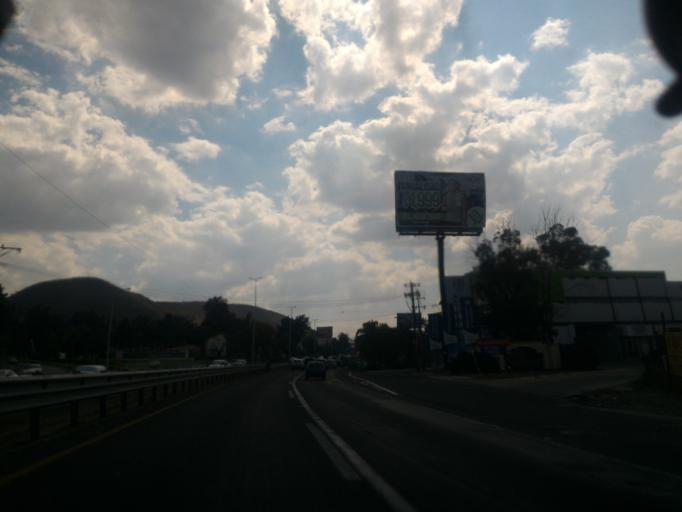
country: MX
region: Jalisco
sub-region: Tlajomulco de Zuniga
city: Lomas de San Agustin
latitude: 20.5333
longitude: -103.4753
